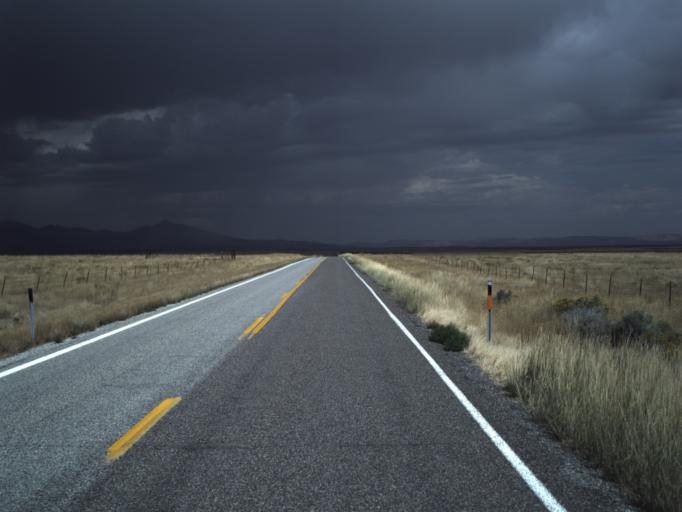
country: US
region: Idaho
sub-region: Oneida County
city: Malad City
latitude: 41.8816
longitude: -113.1170
